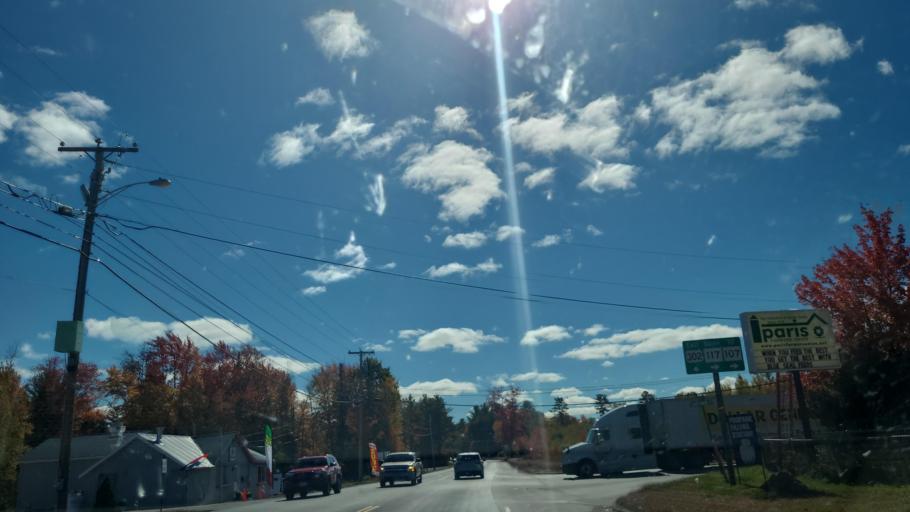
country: US
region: Maine
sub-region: Cumberland County
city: Bridgton
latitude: 44.0329
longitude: -70.6968
